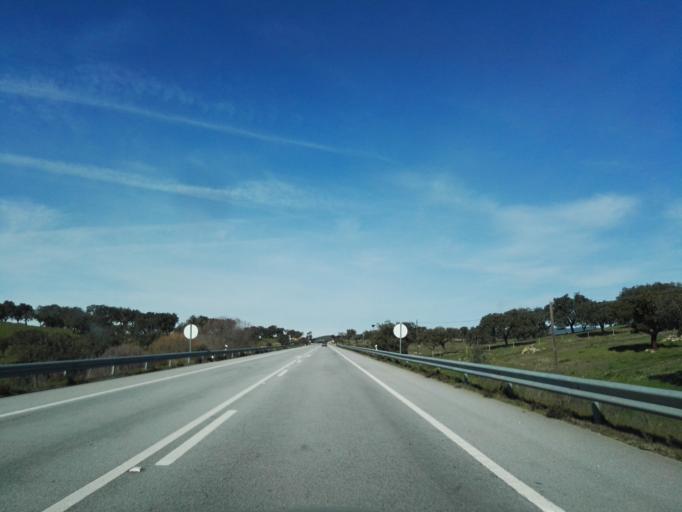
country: PT
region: Portalegre
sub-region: Portalegre
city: Urra
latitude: 39.1995
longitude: -7.3651
